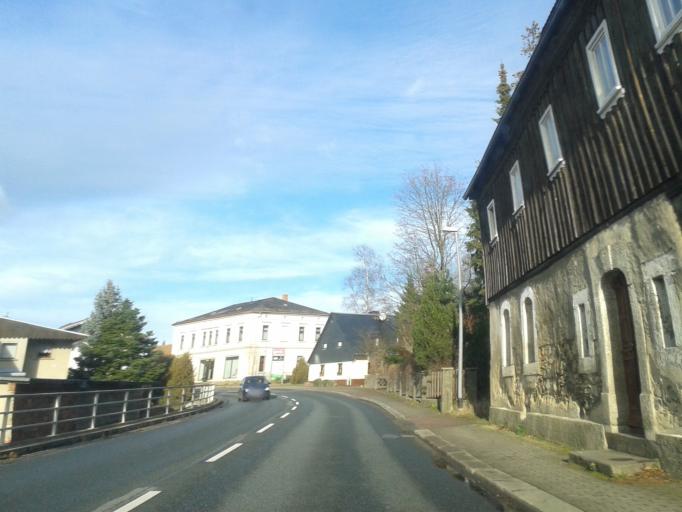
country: DE
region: Saxony
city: Eibau
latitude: 50.9778
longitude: 14.6680
